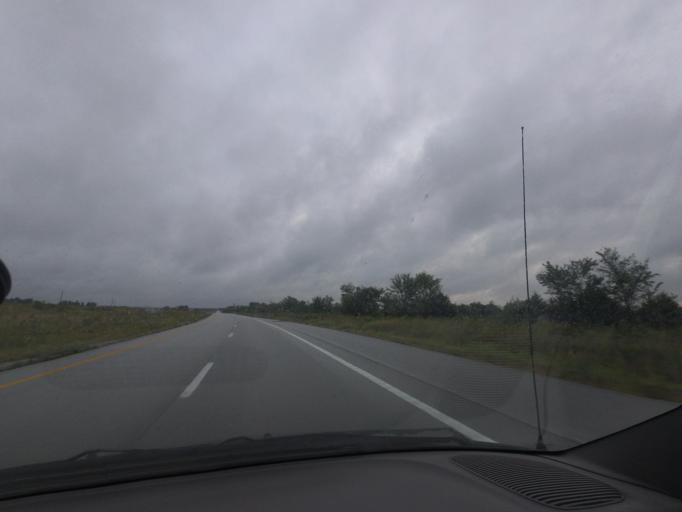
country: US
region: Missouri
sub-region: Marion County
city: Monroe City
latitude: 39.6652
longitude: -91.6759
